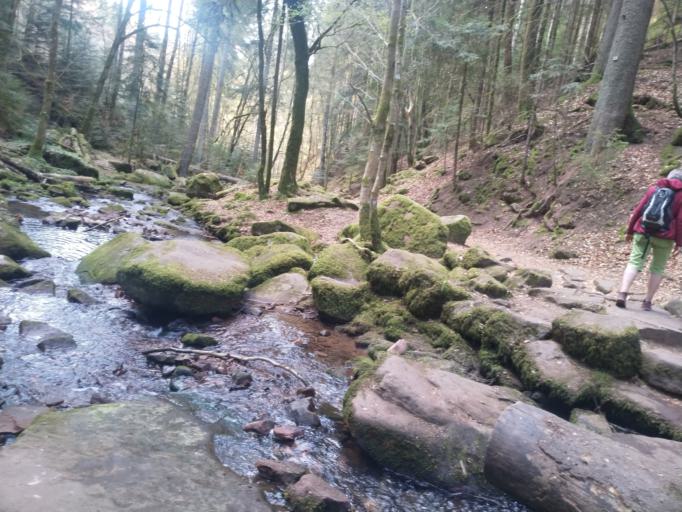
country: DE
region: Baden-Wuerttemberg
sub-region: Karlsruhe Region
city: Bad Liebenzell
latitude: 48.7988
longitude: 8.7443
